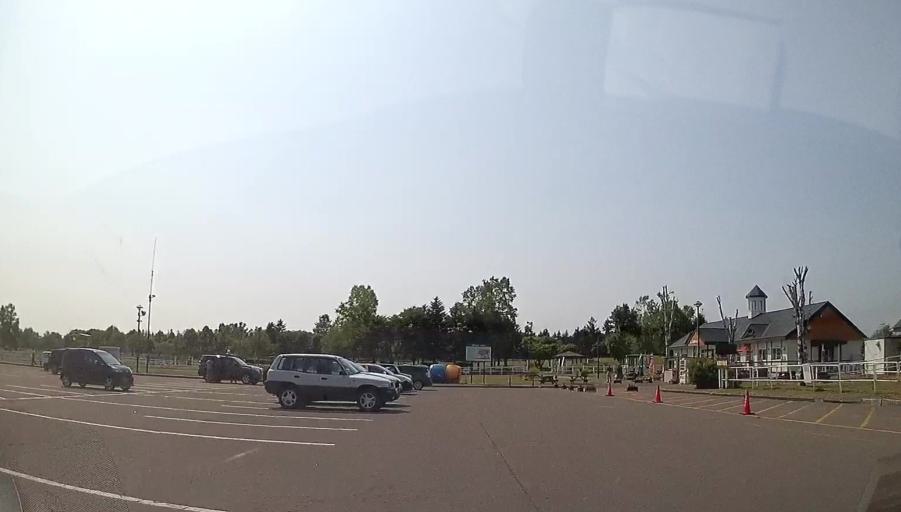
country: JP
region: Hokkaido
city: Otofuke
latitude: 43.1694
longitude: 143.0256
